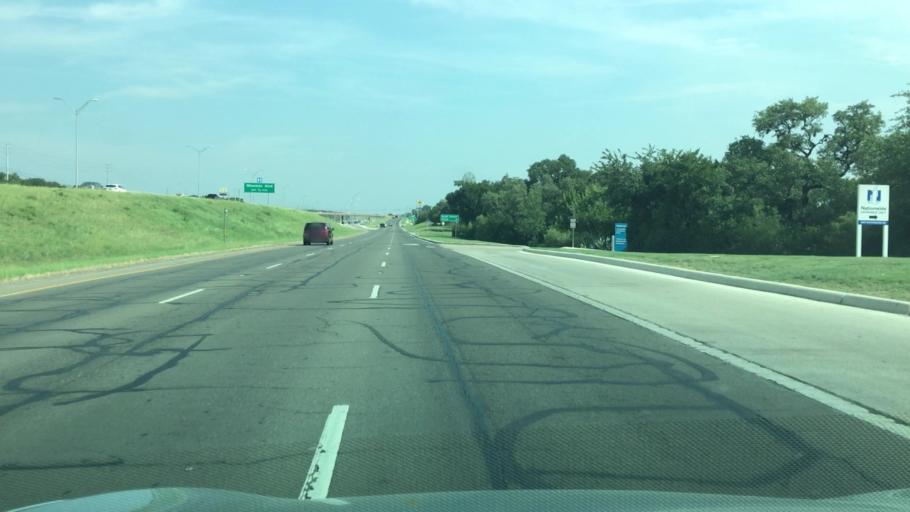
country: US
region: Texas
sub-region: Bexar County
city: Leon Valley
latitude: 29.4562
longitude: -98.6877
